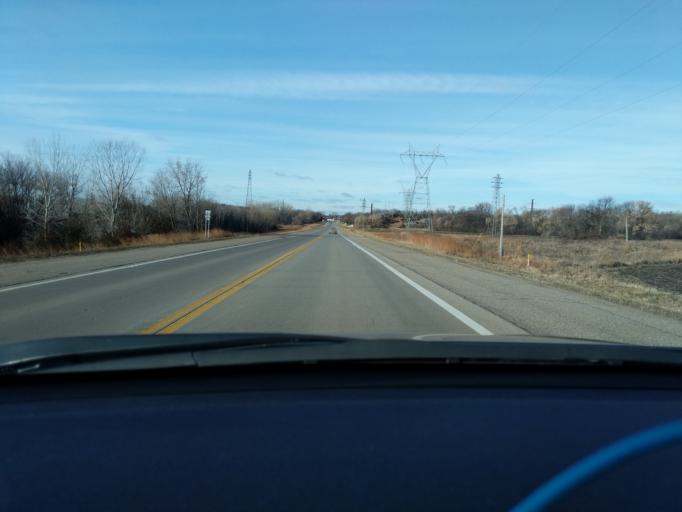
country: US
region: Minnesota
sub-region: Yellow Medicine County
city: Granite Falls
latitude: 44.8048
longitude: -95.5232
